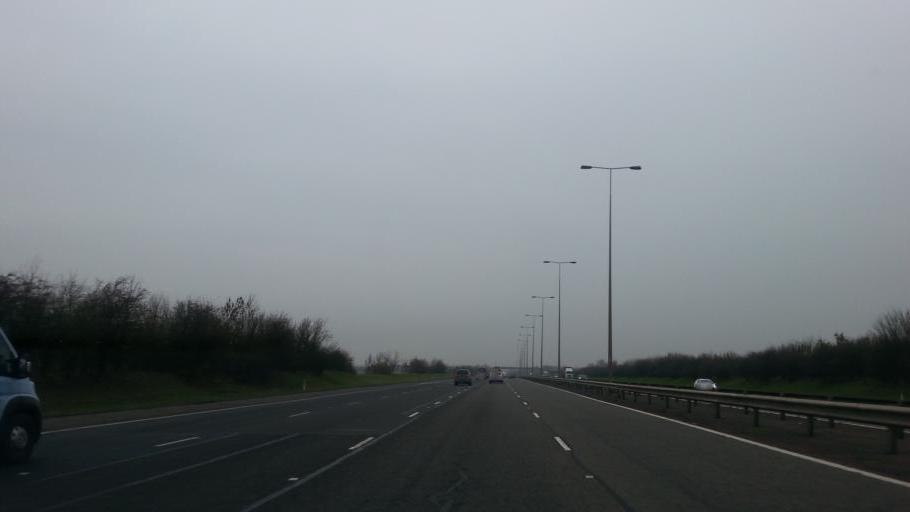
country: GB
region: England
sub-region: Cambridgeshire
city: Sawtry
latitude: 52.4582
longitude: -0.2807
